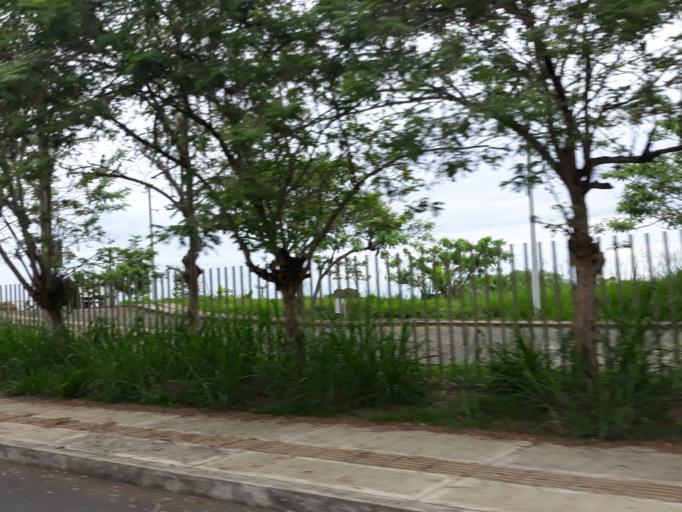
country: CO
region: Valle del Cauca
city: Jamundi
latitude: 3.3467
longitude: -76.5524
